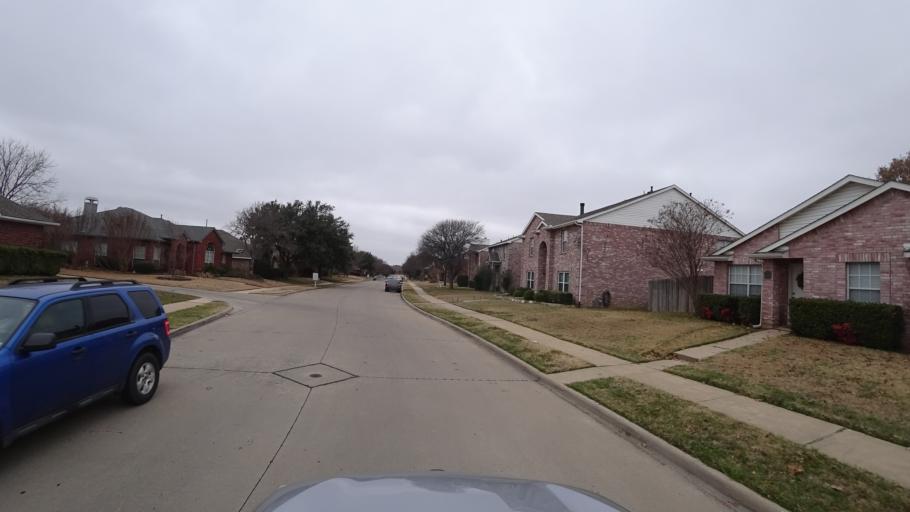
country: US
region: Texas
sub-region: Denton County
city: Lewisville
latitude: 33.0335
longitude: -97.0319
